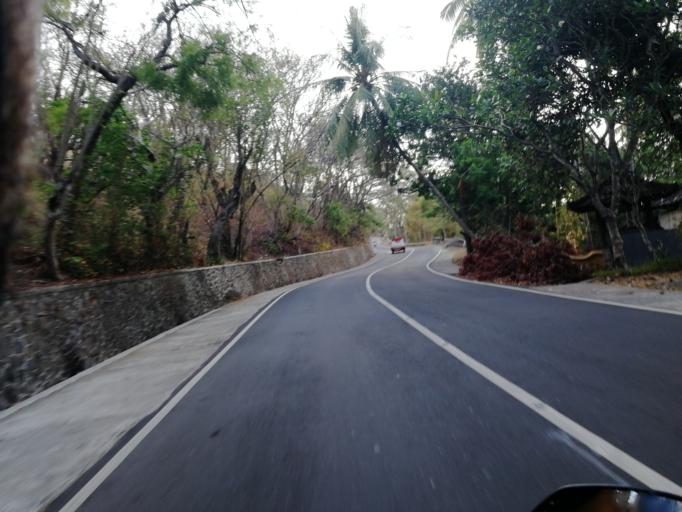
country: ID
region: West Nusa Tenggara
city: Karangsubagan
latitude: -8.4824
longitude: 116.0378
